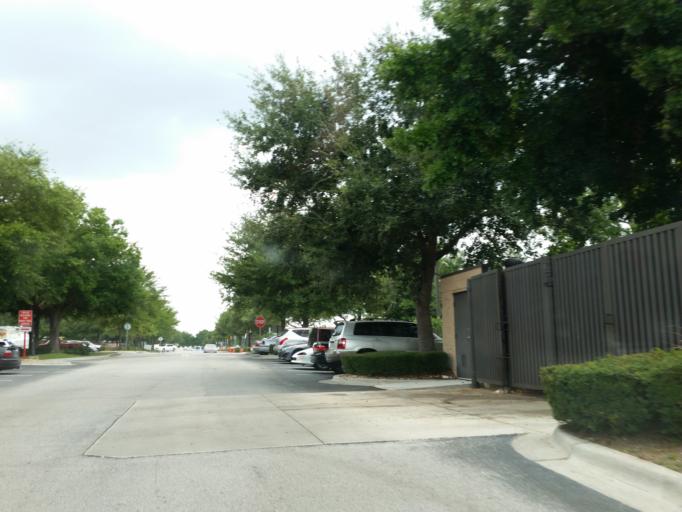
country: US
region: Florida
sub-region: Hillsborough County
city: Brandon
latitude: 27.9388
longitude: -82.2626
